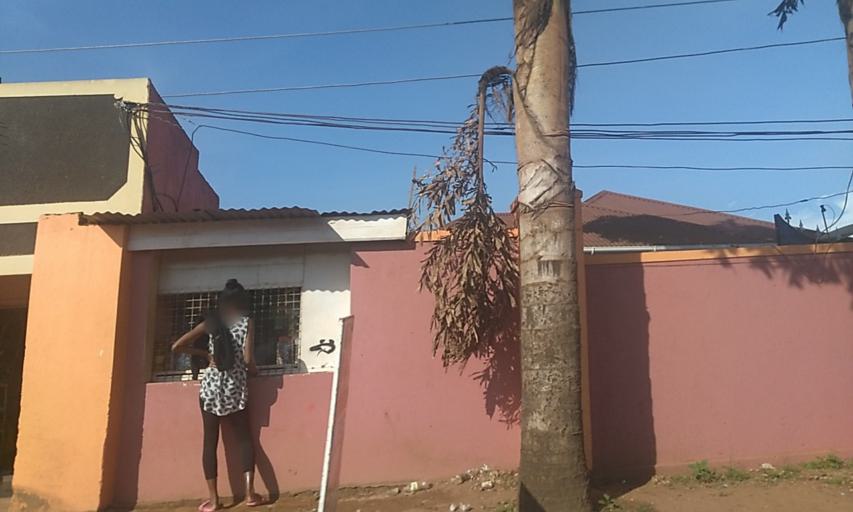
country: UG
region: Central Region
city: Kampala Central Division
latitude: 0.3203
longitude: 32.5467
